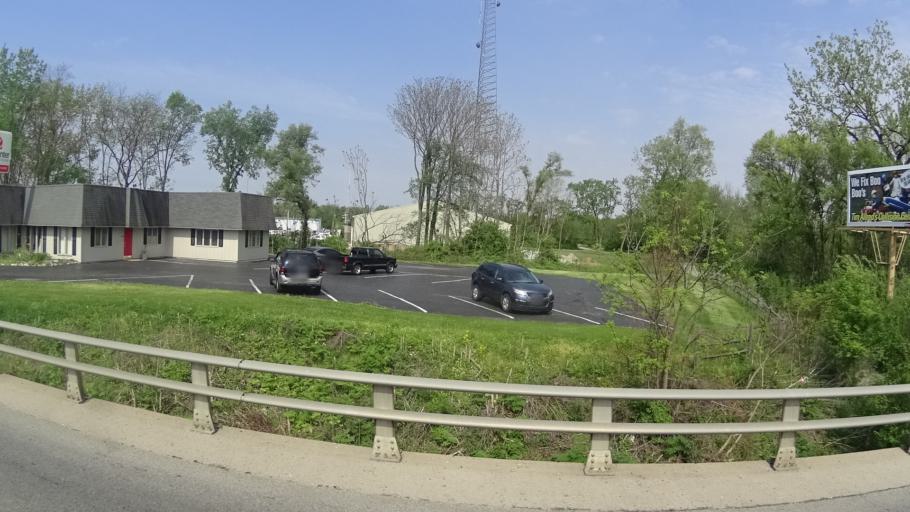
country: US
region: Indiana
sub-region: Madison County
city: Anderson
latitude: 40.1163
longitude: -85.6797
